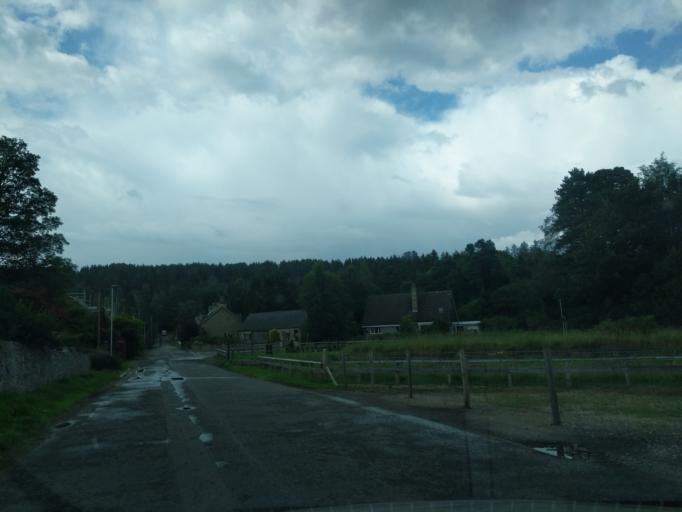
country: GB
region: Scotland
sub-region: Moray
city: Rothes
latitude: 57.4554
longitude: -3.2998
